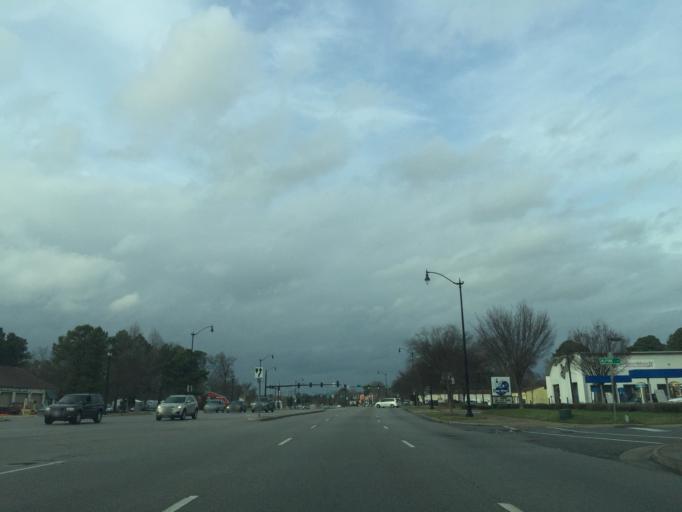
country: US
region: Virginia
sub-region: City of Newport News
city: Newport News
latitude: 37.0815
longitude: -76.4975
